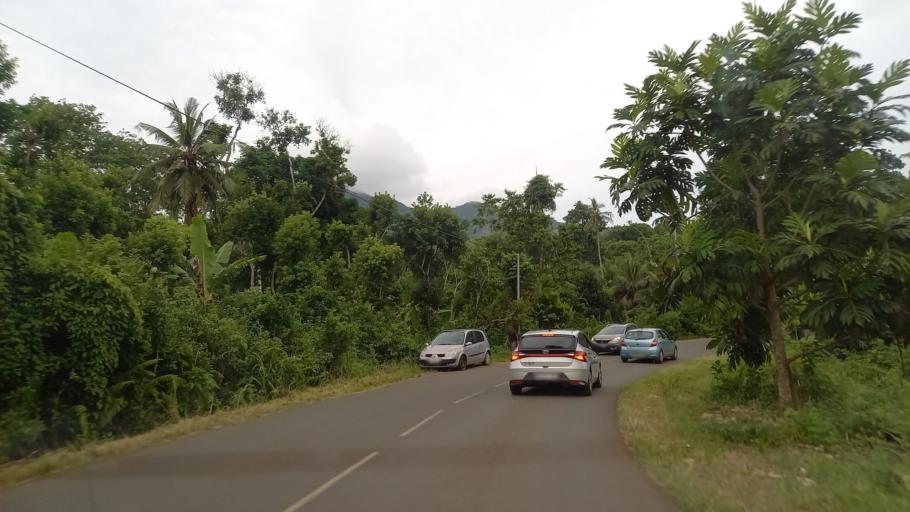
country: YT
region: Chirongui
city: Chirongui
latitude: -12.8986
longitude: 45.1458
